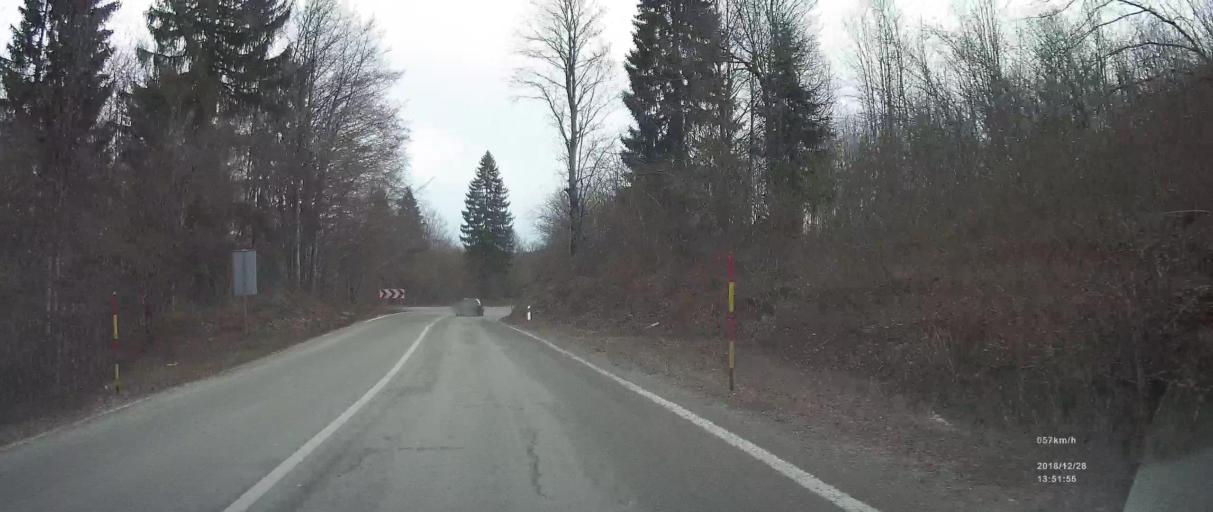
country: HR
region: Primorsko-Goranska
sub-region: Grad Delnice
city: Delnice
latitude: 45.3936
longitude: 14.8440
